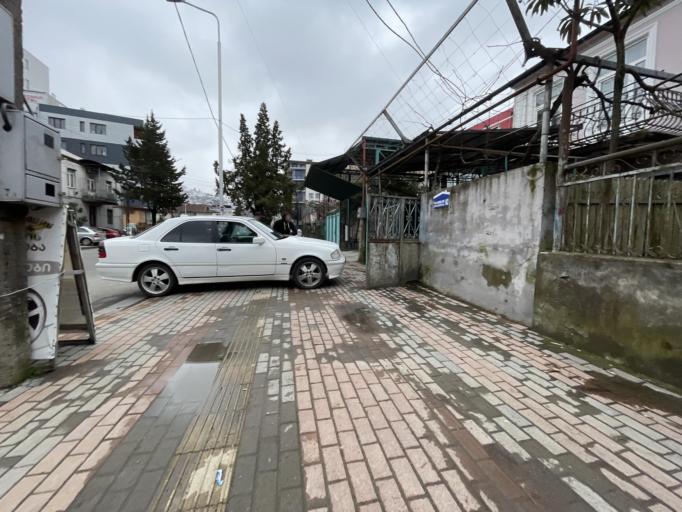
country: GE
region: Ajaria
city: Batumi
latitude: 41.6380
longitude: 41.6416
